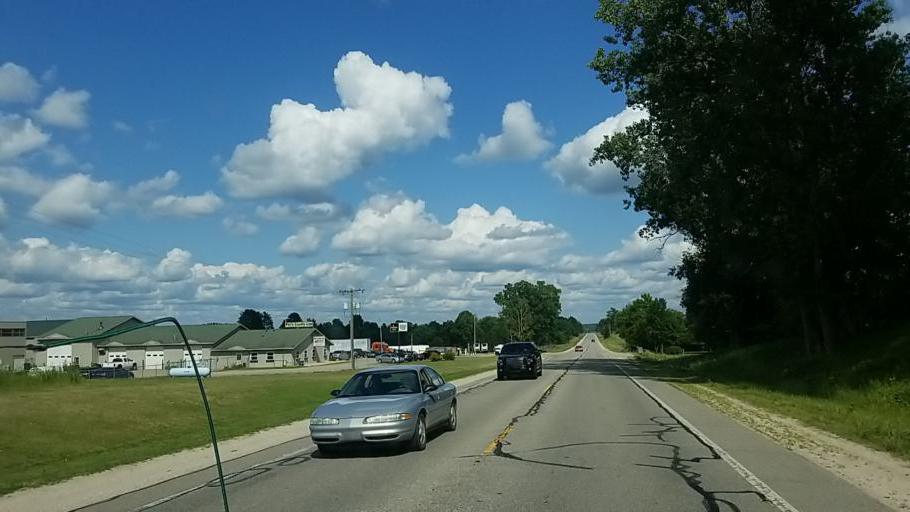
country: US
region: Michigan
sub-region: Osceola County
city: Reed City
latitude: 43.8876
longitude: -85.5582
